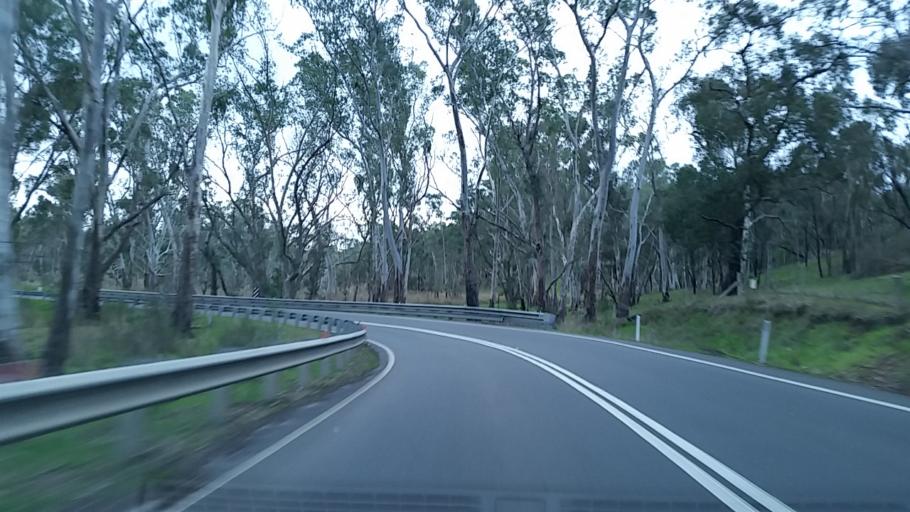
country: AU
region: South Australia
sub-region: Adelaide Hills
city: Gumeracha
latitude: -34.8156
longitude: 138.8129
